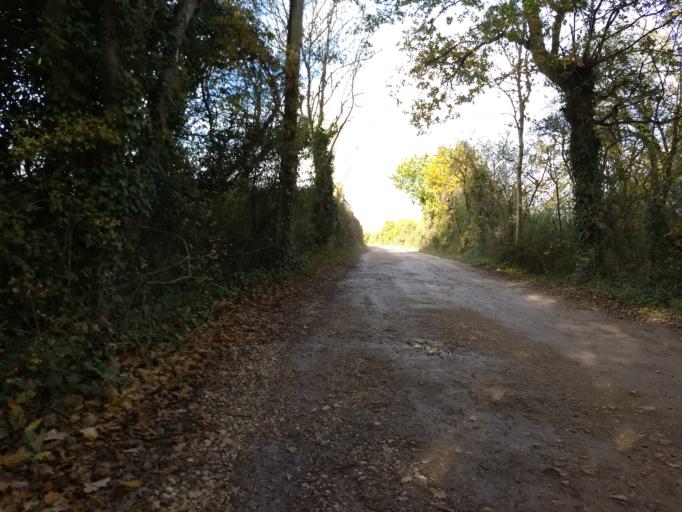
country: GB
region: England
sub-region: Isle of Wight
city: Freshwater
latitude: 50.7019
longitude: -1.5094
